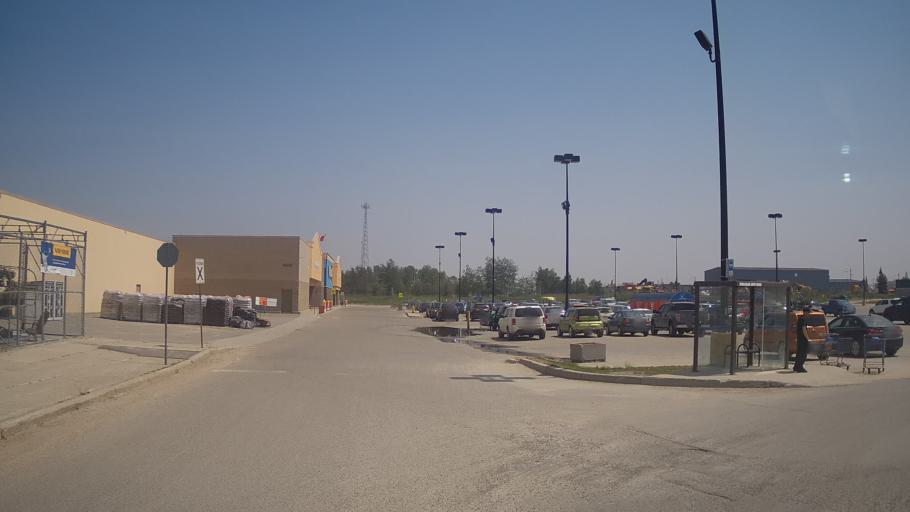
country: CA
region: Ontario
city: Timmins
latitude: 48.4743
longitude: -81.3949
